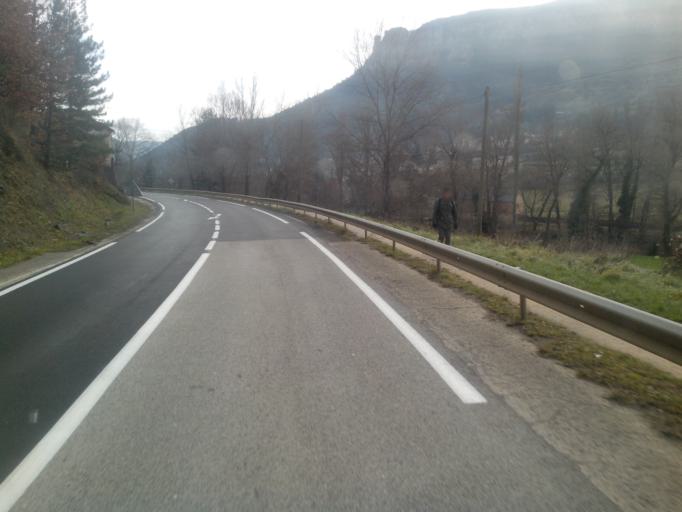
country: FR
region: Languedoc-Roussillon
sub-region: Departement de la Lozere
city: Florac
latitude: 44.3349
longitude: 3.5861
